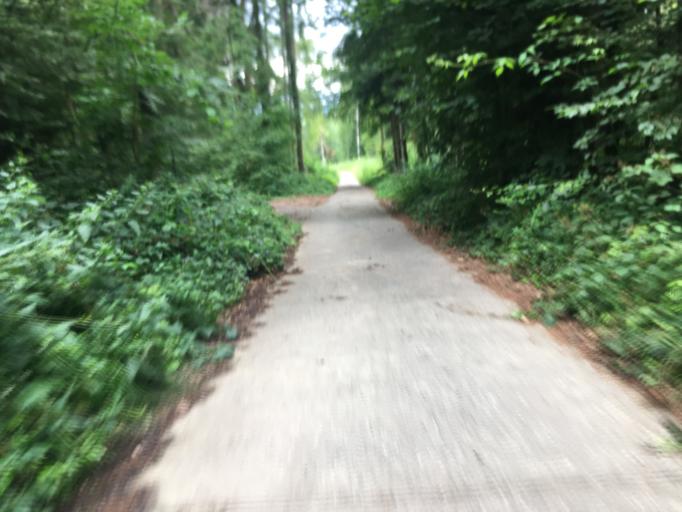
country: CH
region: Fribourg
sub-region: Broye District
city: Estavayer-le-Lac
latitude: 46.8705
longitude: 6.8986
